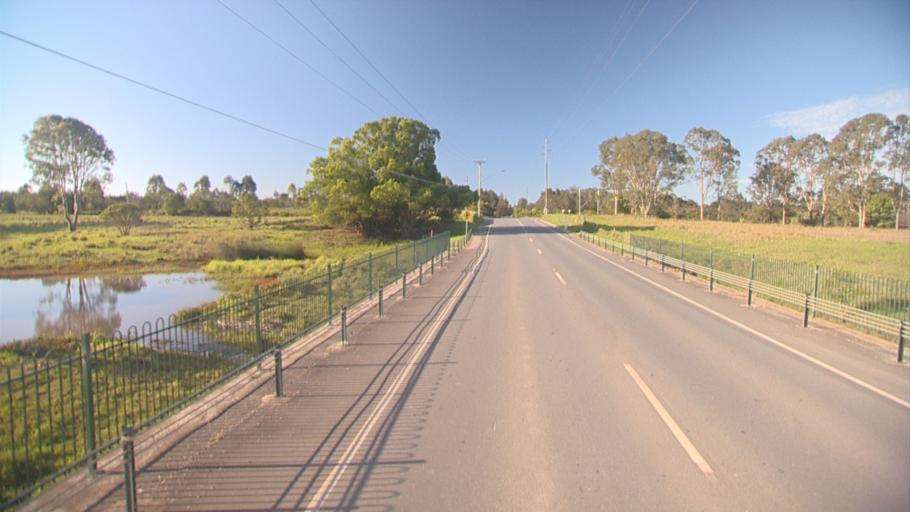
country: AU
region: Queensland
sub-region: Logan
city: Waterford West
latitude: -27.7010
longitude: 153.1179
